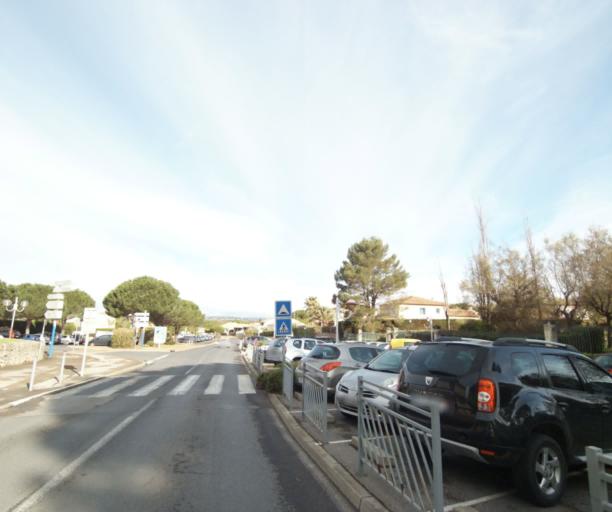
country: FR
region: Languedoc-Roussillon
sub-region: Departement de l'Herault
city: Saint-Jean-de-Vedas
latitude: 43.5789
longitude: 3.8240
